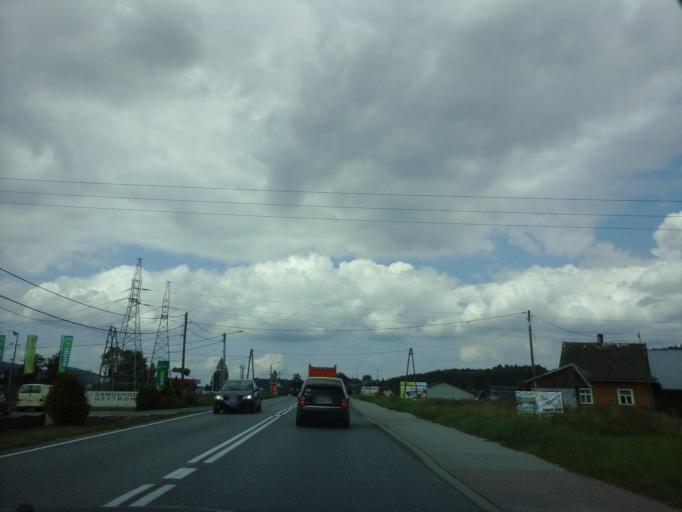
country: PL
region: Lesser Poland Voivodeship
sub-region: Powiat suski
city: Jordanow
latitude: 49.6539
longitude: 19.8179
